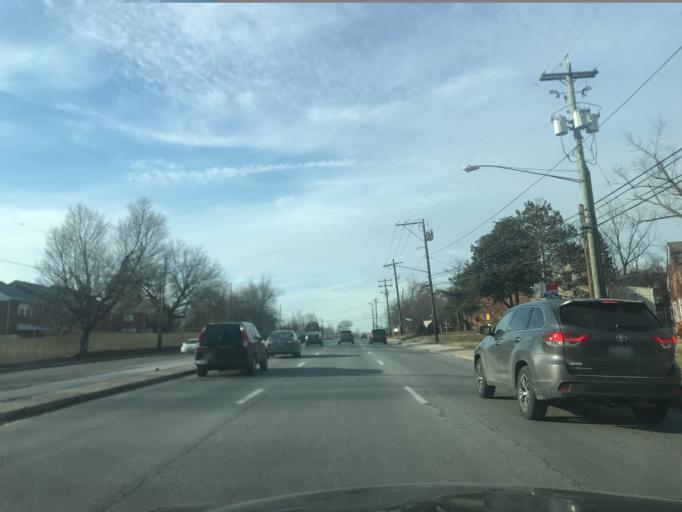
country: US
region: Maryland
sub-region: Montgomery County
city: Glenmont
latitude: 39.0653
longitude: -77.0576
